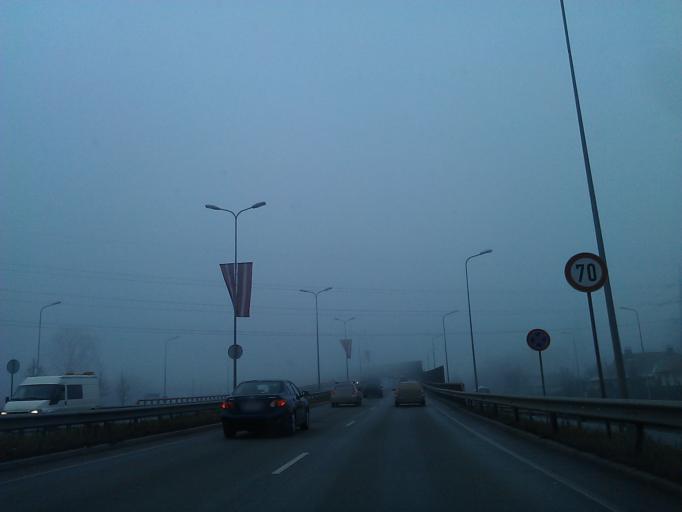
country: LV
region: Riga
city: Riga
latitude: 56.9311
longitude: 24.1882
